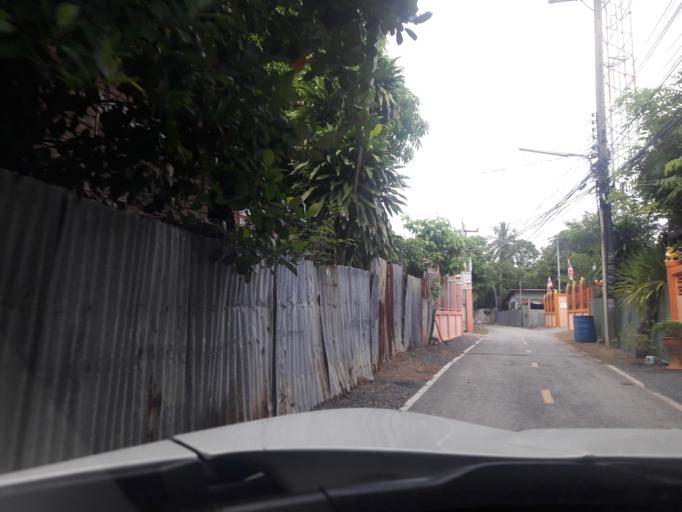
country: TH
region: Lop Buri
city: Ban Mi
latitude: 15.0459
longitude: 100.5476
